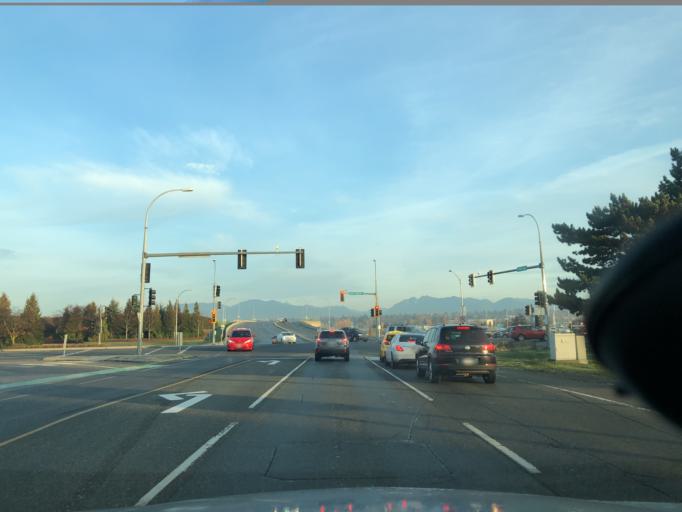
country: CA
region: British Columbia
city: Richmond
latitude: 49.1924
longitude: -123.1507
